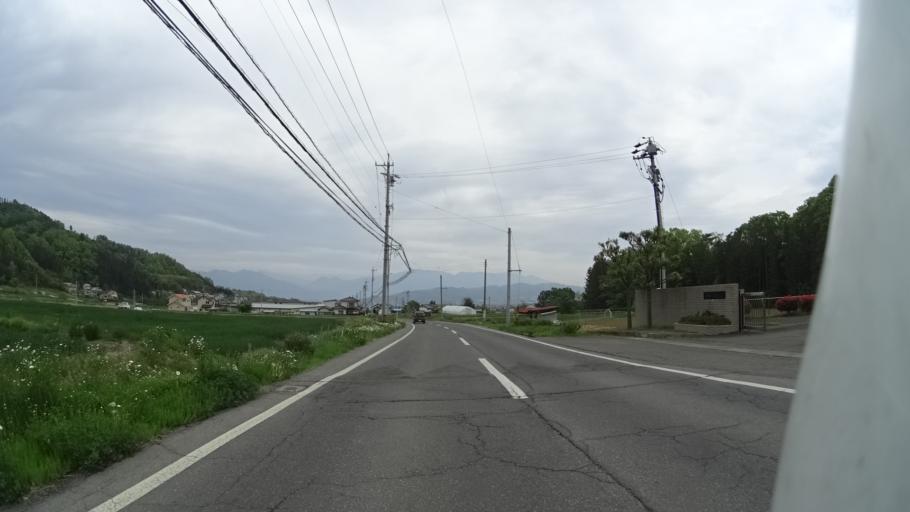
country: JP
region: Nagano
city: Kamimaruko
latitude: 36.3564
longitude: 138.1673
